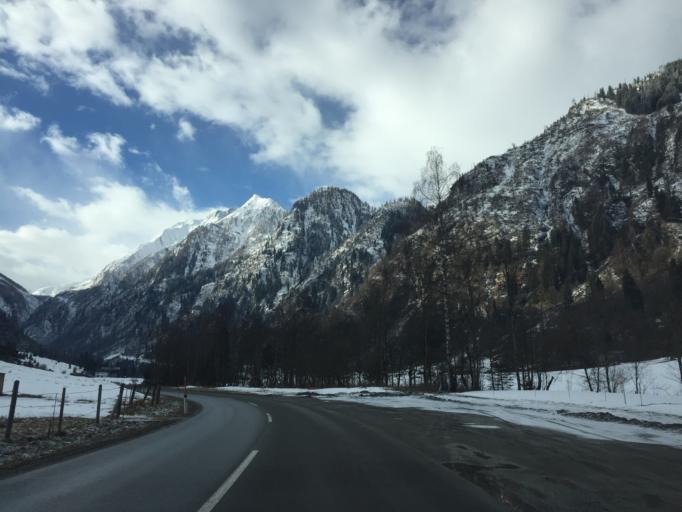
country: AT
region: Salzburg
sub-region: Politischer Bezirk Zell am See
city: Kaprun
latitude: 47.2485
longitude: 12.7360
